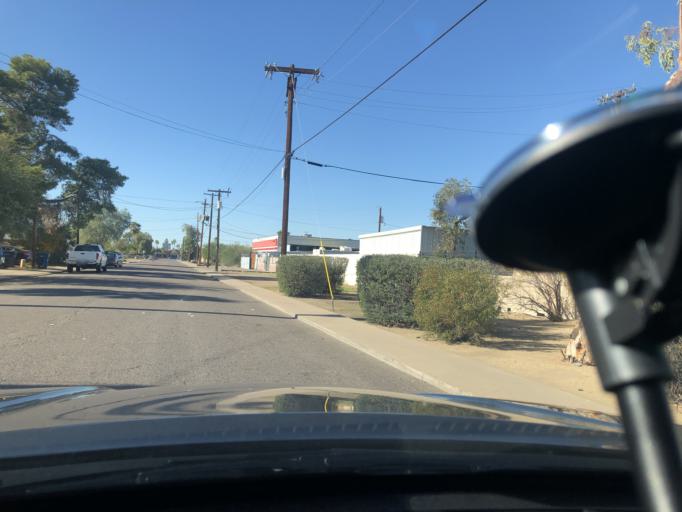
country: US
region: Arizona
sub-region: Maricopa County
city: Phoenix
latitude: 33.4649
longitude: -112.0240
